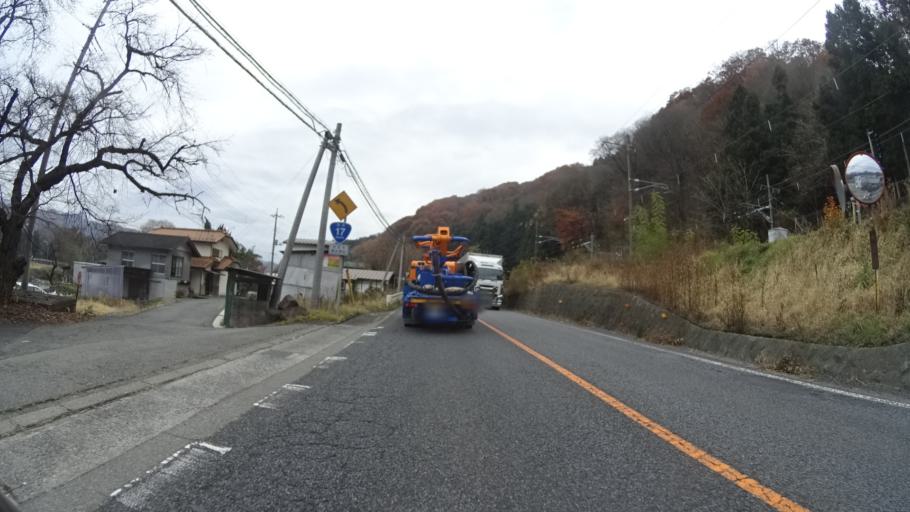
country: JP
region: Gunma
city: Numata
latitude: 36.6113
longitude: 139.0415
